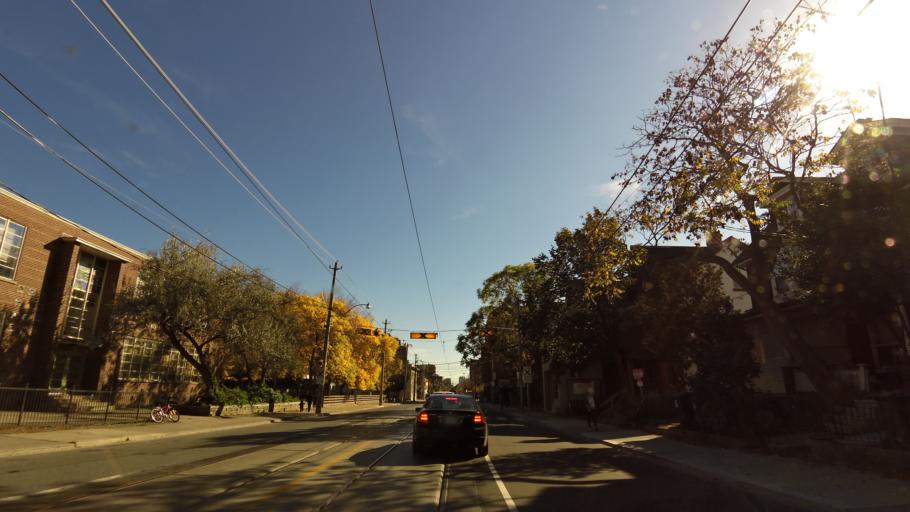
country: CA
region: Ontario
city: Toronto
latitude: 43.6580
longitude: -79.4084
